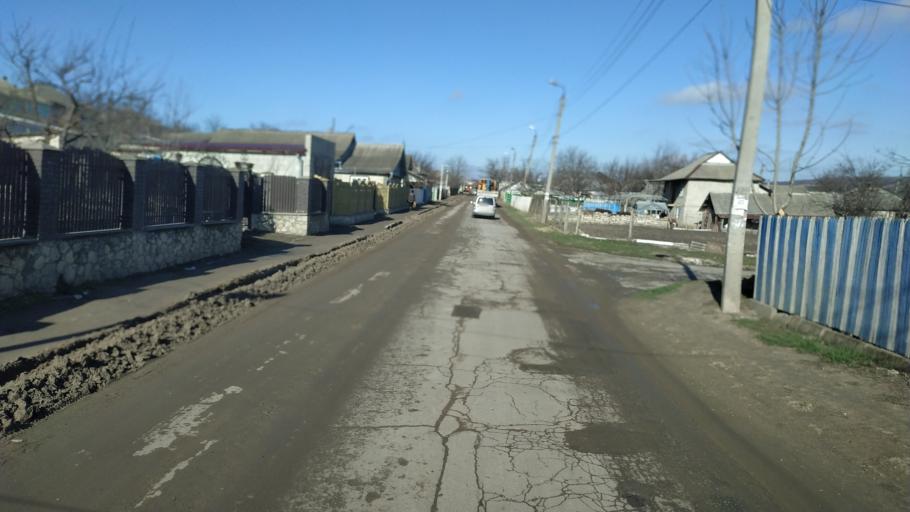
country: MD
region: Hincesti
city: Hincesti
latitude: 46.9317
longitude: 28.6477
